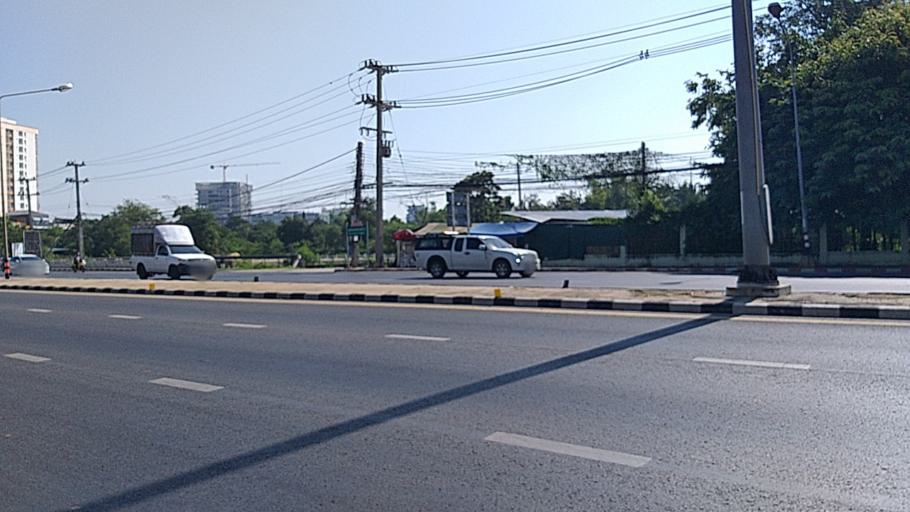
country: TH
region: Nakhon Ratchasima
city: Nakhon Ratchasima
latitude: 14.9838
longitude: 102.0925
